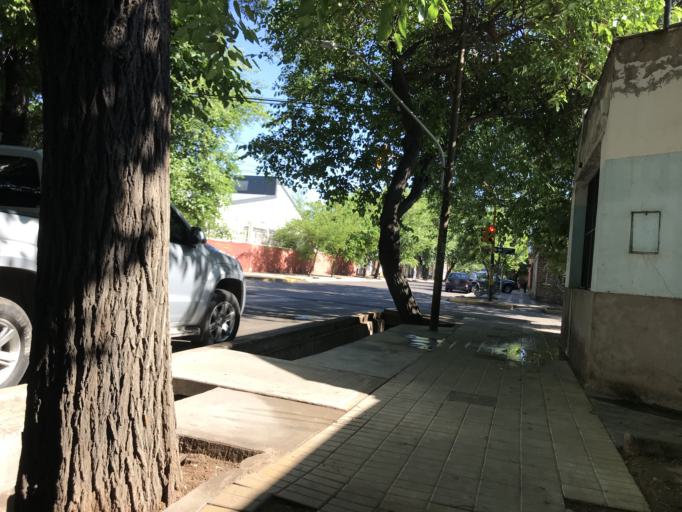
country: AR
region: Mendoza
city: Mendoza
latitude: -32.8782
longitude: -68.8308
